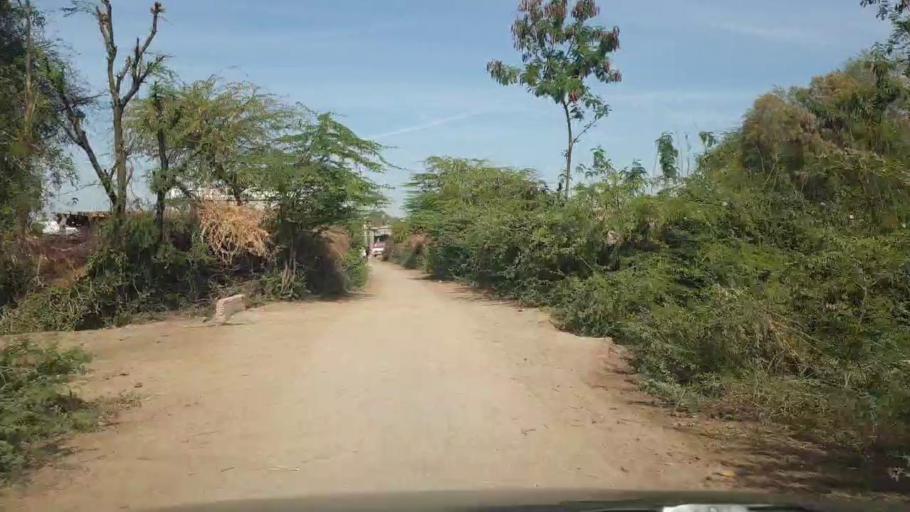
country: PK
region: Sindh
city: Umarkot
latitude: 25.3633
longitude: 69.6105
